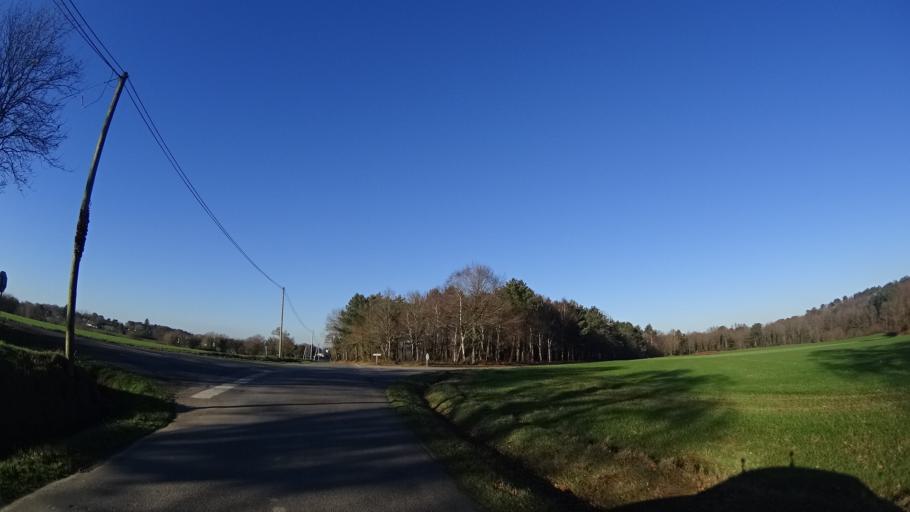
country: FR
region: Brittany
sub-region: Departement du Morbihan
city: Allaire
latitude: 47.6466
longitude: -2.1788
